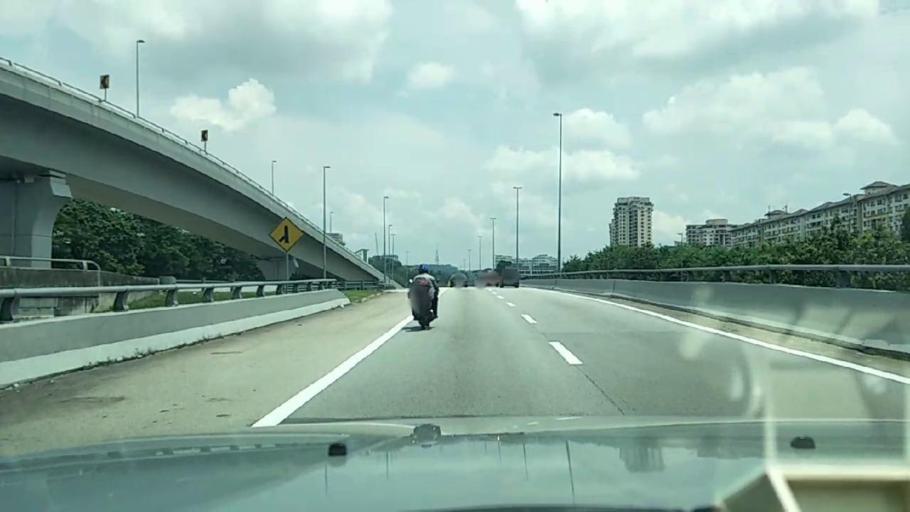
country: MY
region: Kuala Lumpur
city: Kuala Lumpur
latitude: 3.0944
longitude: 101.6893
